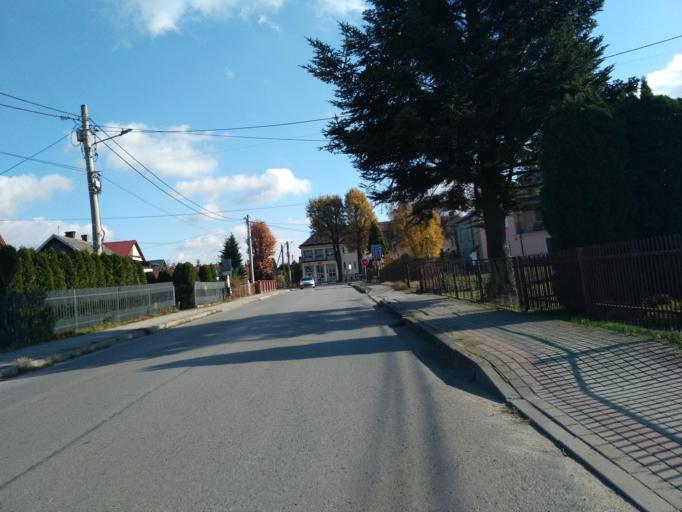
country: PL
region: Subcarpathian Voivodeship
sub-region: Powiat rzeszowski
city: Swilcza
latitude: 50.1150
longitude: 21.8970
